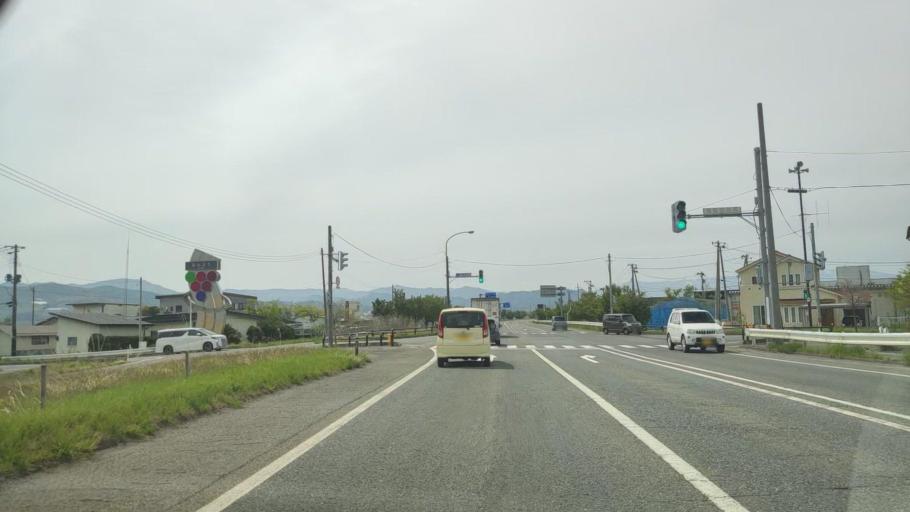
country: JP
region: Yamagata
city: Takahata
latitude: 38.0497
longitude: 140.1742
